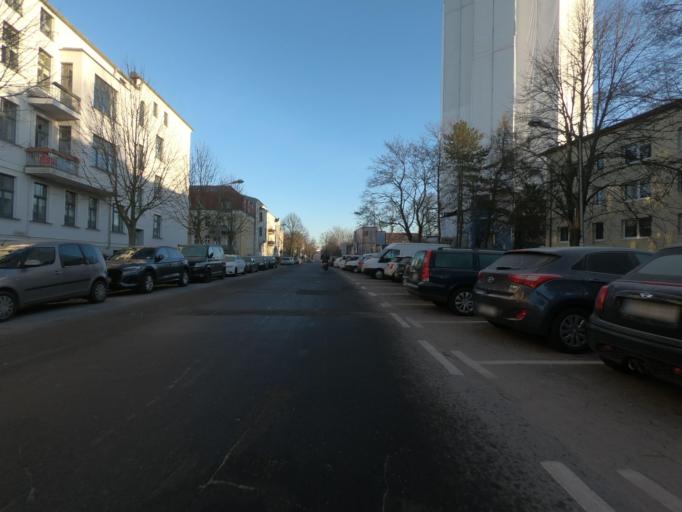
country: DE
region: Mecklenburg-Vorpommern
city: Rostock
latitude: 54.0769
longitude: 12.1416
